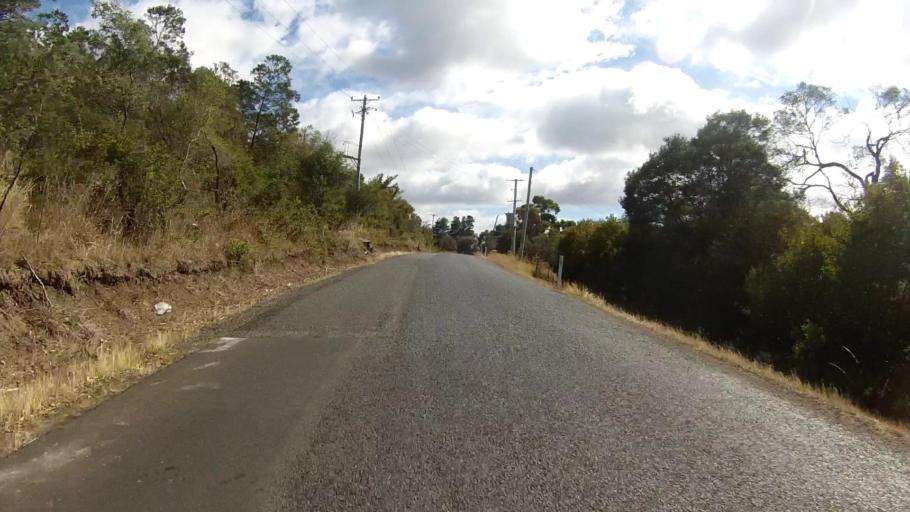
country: AU
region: Tasmania
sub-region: Brighton
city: Old Beach
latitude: -42.7740
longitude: 147.2876
